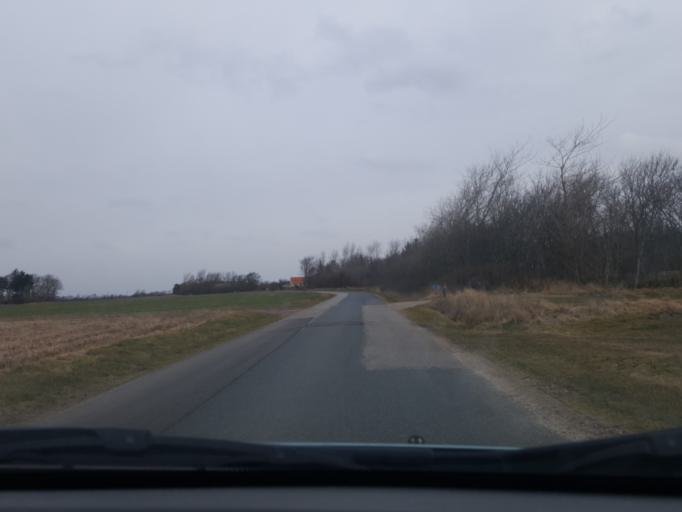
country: DK
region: Central Jutland
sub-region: Holstebro Kommune
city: Ulfborg
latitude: 56.2132
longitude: 8.2600
